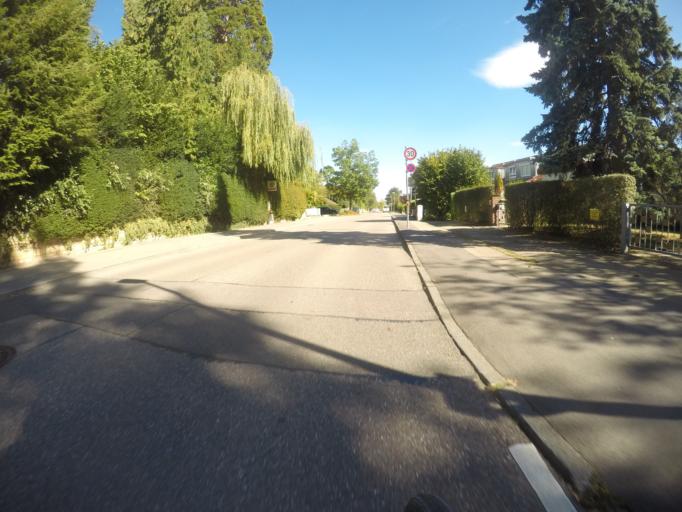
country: DE
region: Baden-Wuerttemberg
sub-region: Regierungsbezirk Stuttgart
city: Stuttgart-Ost
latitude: 48.7613
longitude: 9.2144
